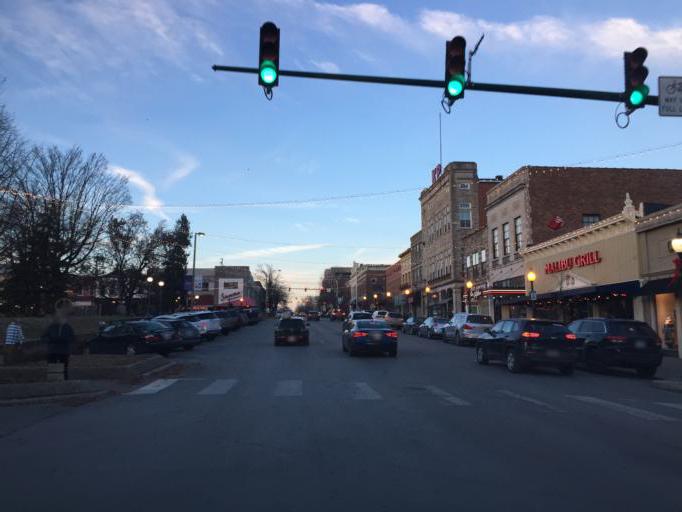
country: US
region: Indiana
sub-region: Monroe County
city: Bloomington
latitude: 39.1665
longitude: -86.5336
